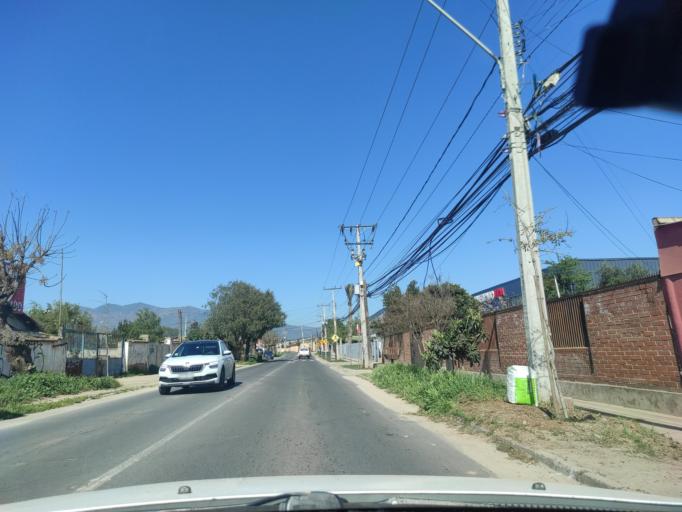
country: CL
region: Valparaiso
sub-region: Provincia de Marga Marga
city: Limache
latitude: -33.0109
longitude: -71.2522
